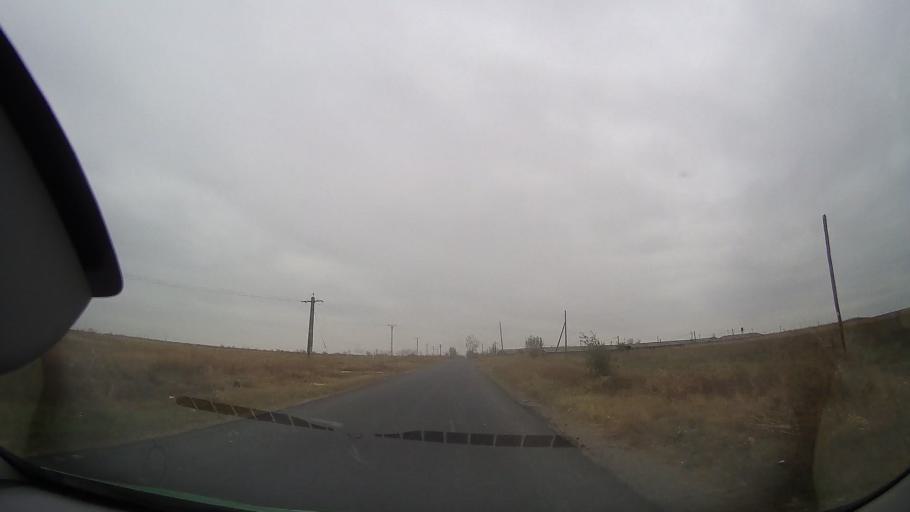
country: RO
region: Braila
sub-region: Comuna Ciocile
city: Ciocile
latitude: 44.8146
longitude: 27.2624
